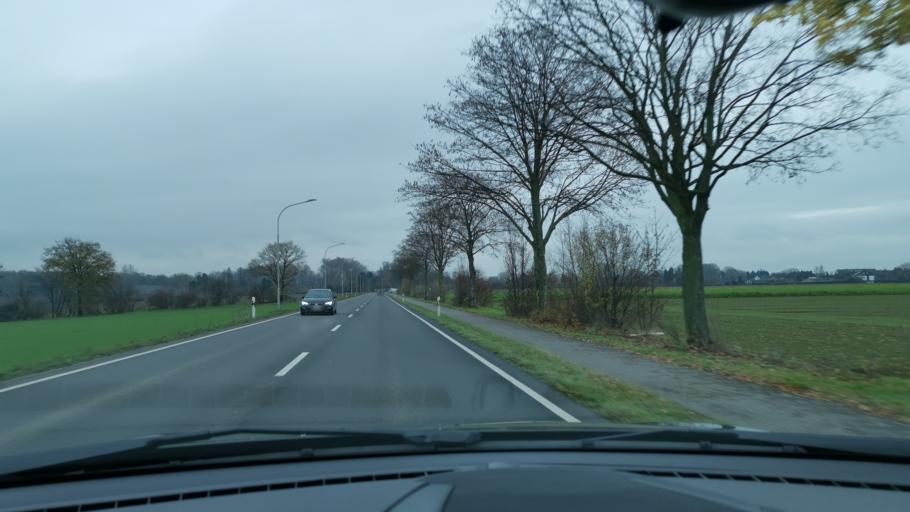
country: DE
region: North Rhine-Westphalia
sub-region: Regierungsbezirk Dusseldorf
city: Neubrueck
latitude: 51.1136
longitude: 6.6393
